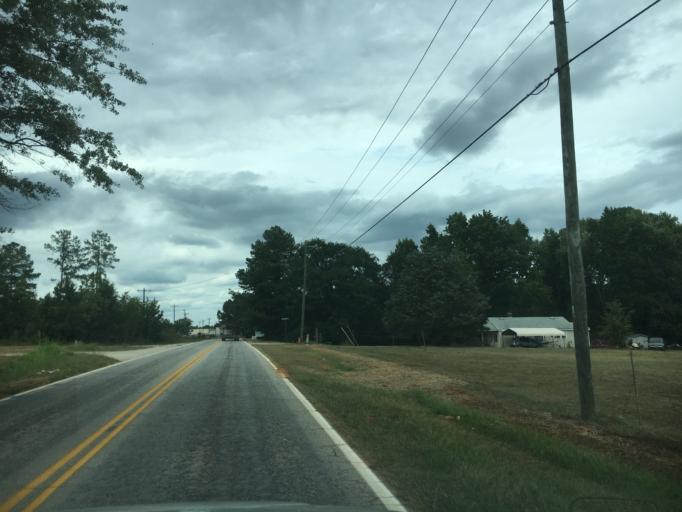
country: US
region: South Carolina
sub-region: Laurens County
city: Watts Mills
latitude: 34.4996
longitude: -81.9727
